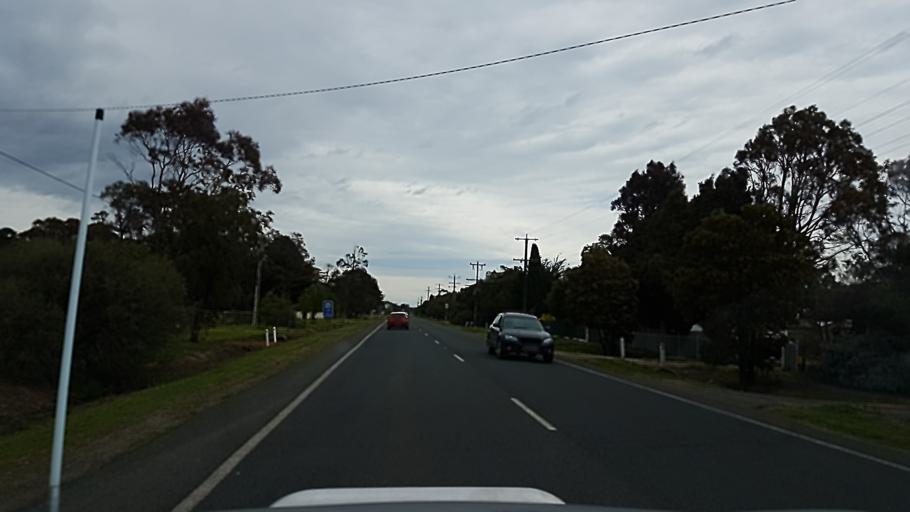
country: AU
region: Victoria
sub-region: Ballarat North
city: Mount Clear
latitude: -37.8507
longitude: 144.0764
